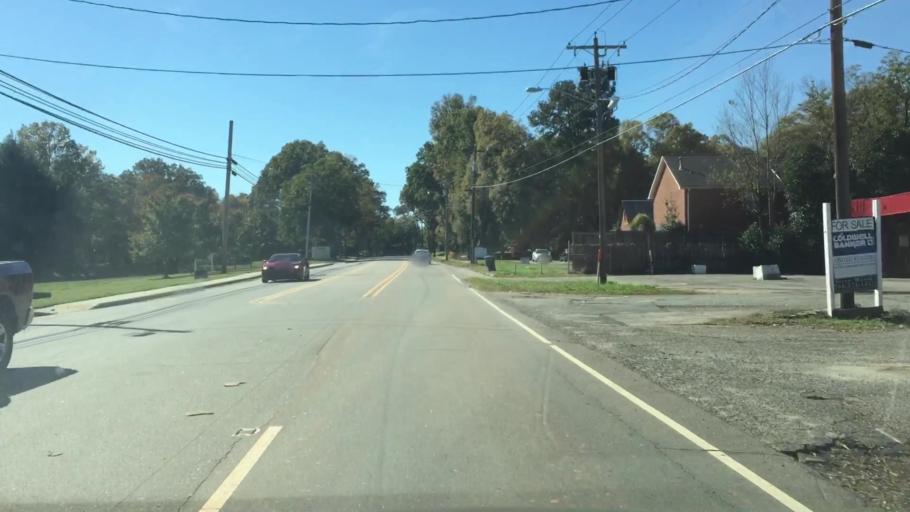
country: US
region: North Carolina
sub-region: Iredell County
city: Mooresville
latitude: 35.5892
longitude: -80.7956
